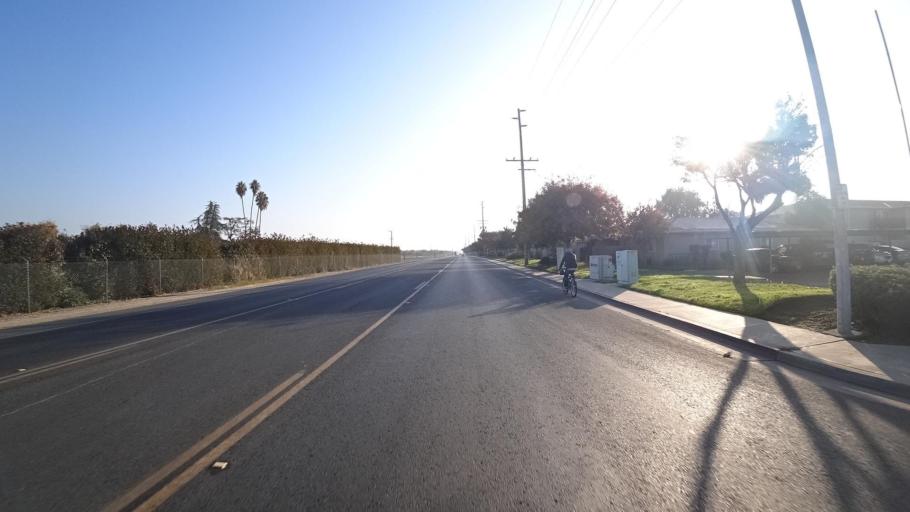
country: US
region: California
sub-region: Kern County
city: Delano
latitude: 35.7904
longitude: -119.2457
